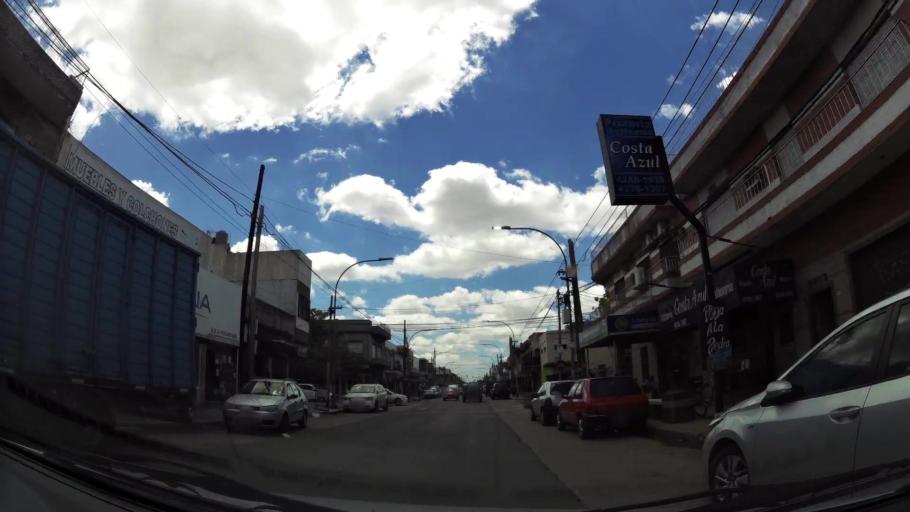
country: AR
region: Buenos Aires
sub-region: Partido de Lanus
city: Lanus
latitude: -34.7111
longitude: -58.4235
